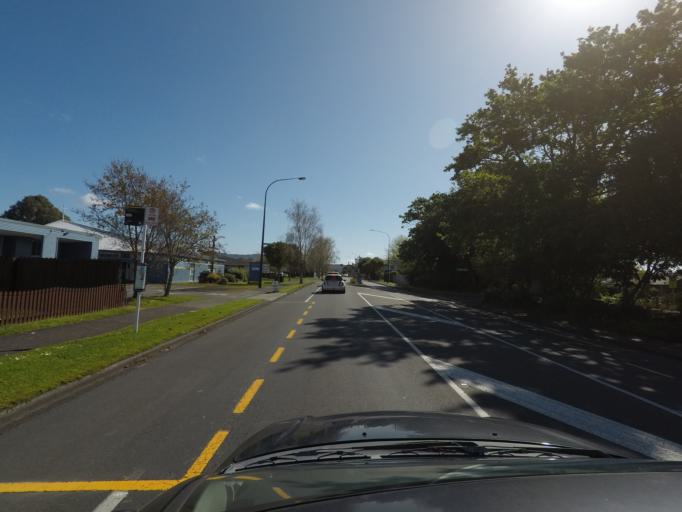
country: NZ
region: Auckland
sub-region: Auckland
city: Rosebank
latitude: -36.8637
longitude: 174.6044
